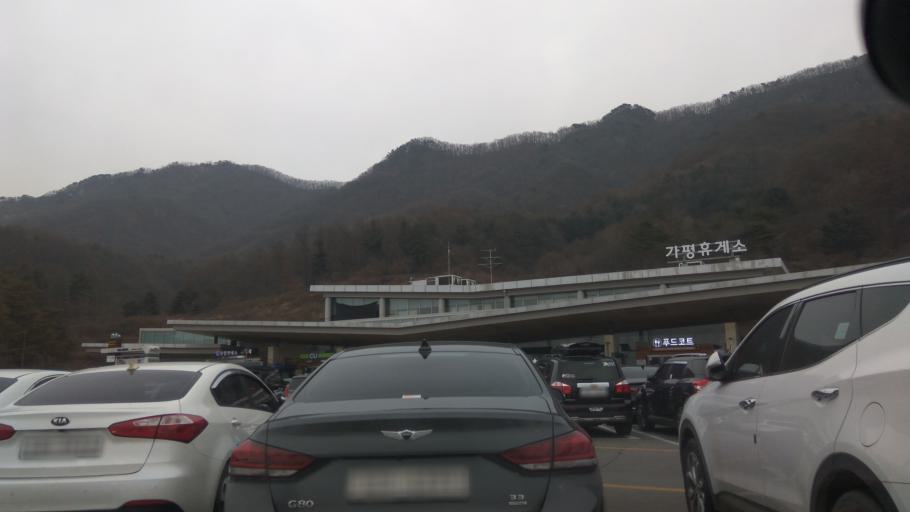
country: KR
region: Gyeonggi-do
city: Cheongpyeong
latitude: 37.7021
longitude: 127.5461
